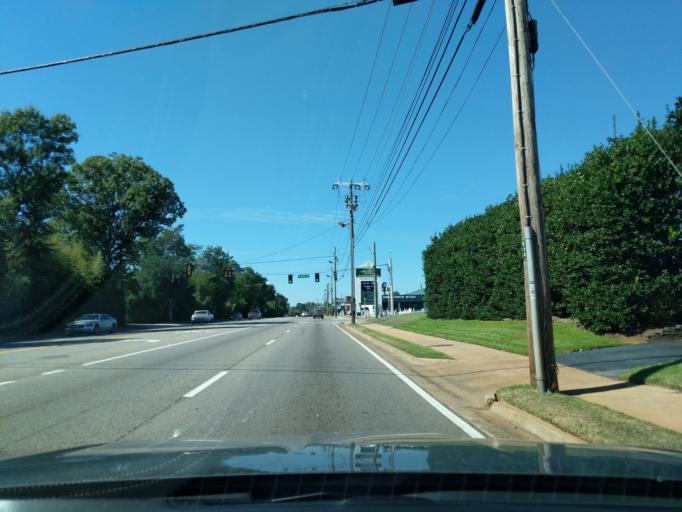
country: US
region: South Carolina
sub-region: Aiken County
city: North Augusta
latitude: 33.5062
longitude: -82.0187
